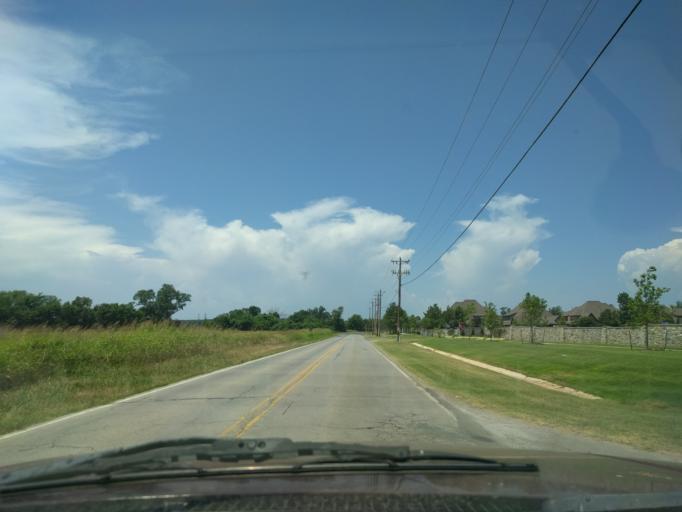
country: US
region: Oklahoma
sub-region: Tulsa County
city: Jenks
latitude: 35.9884
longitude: -95.9250
